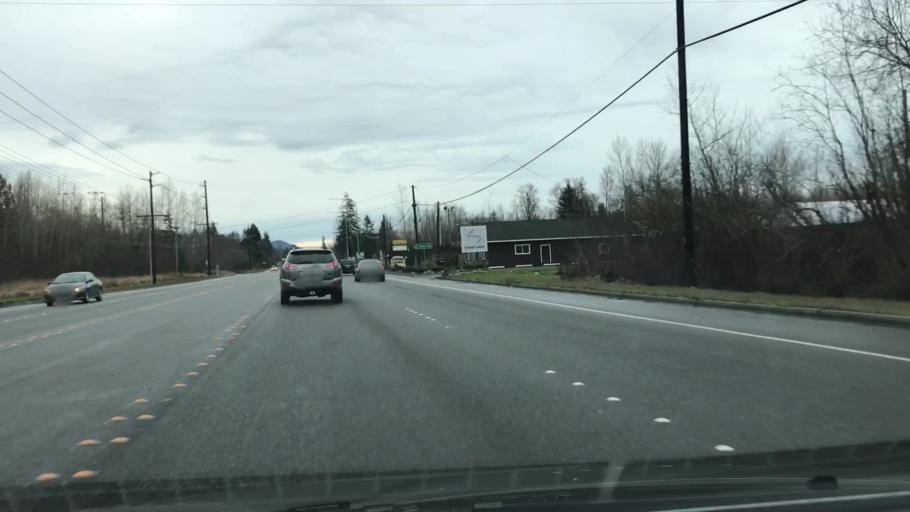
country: US
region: Washington
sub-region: Whatcom County
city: Bellingham
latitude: 48.8168
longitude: -122.4861
